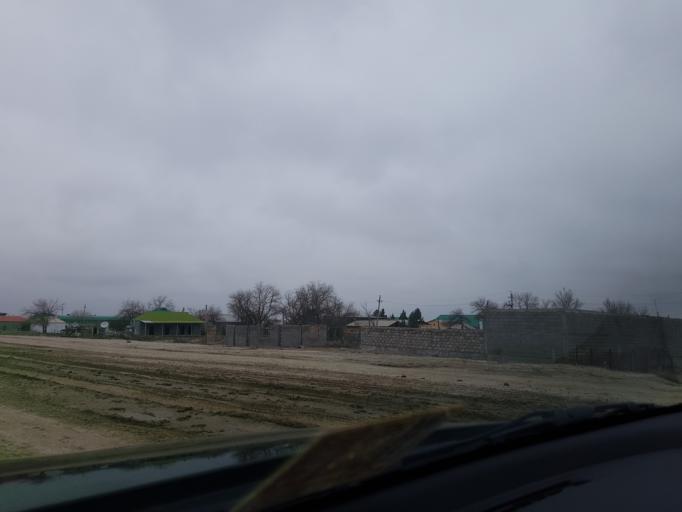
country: TM
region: Ahal
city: Abadan
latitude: 38.1441
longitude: 57.9619
